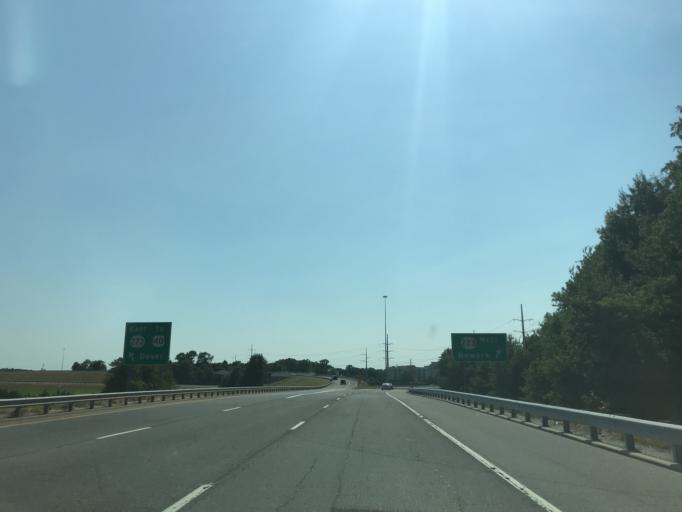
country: US
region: Delaware
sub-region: New Castle County
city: Bear
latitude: 39.6753
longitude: -75.6739
